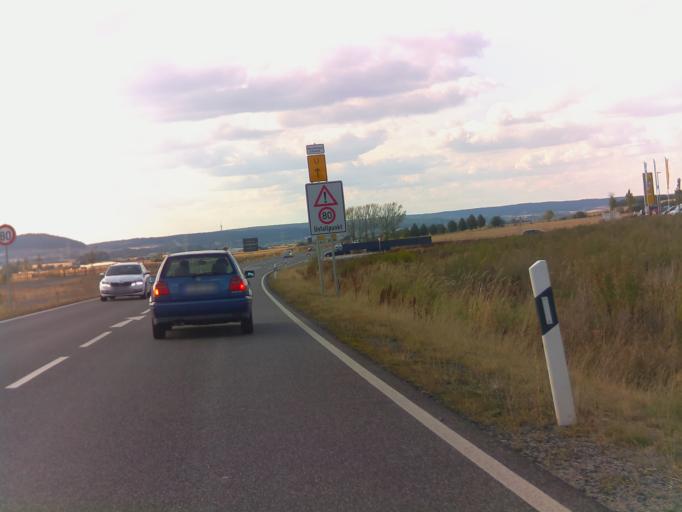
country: DE
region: Hesse
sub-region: Regierungsbezirk Kassel
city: Dipperz
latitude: 50.5392
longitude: 9.7880
